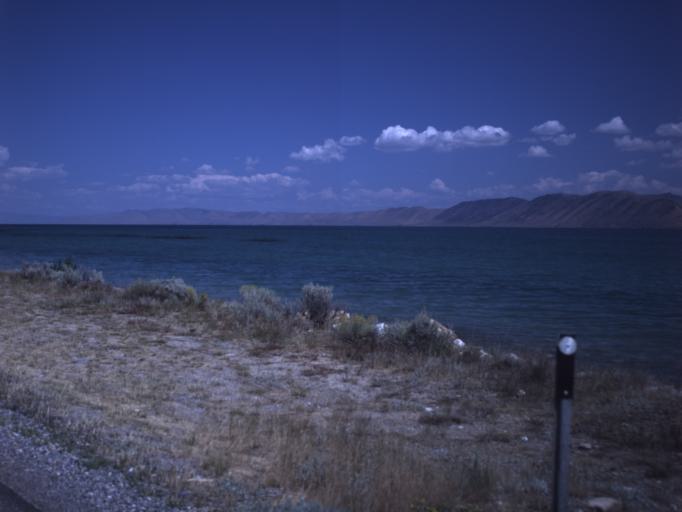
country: US
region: Utah
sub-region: Rich County
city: Randolph
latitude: 41.8790
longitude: -111.3656
